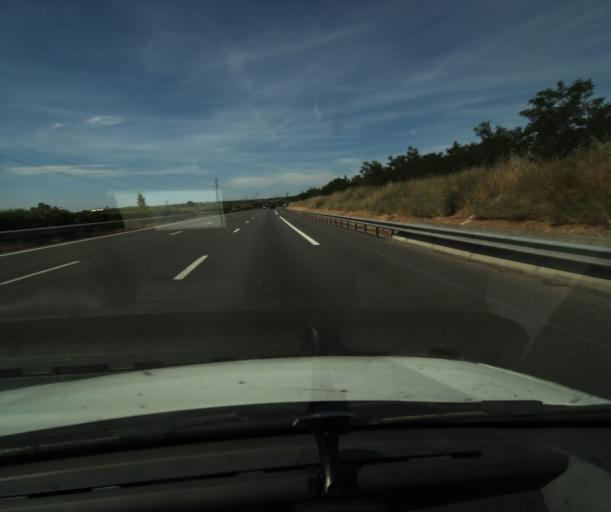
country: FR
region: Midi-Pyrenees
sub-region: Departement de la Haute-Garonne
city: Saint-Sauveur
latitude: 43.7490
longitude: 1.3870
